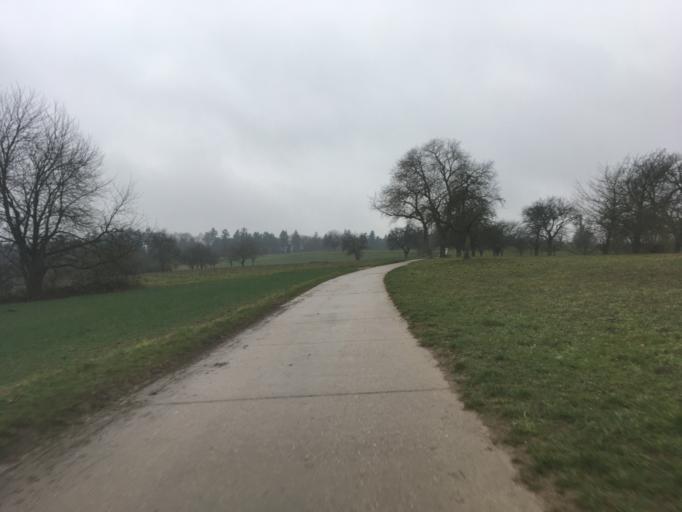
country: DE
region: Baden-Wuerttemberg
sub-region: Karlsruhe Region
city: Ettlingen
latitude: 48.9752
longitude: 8.4850
